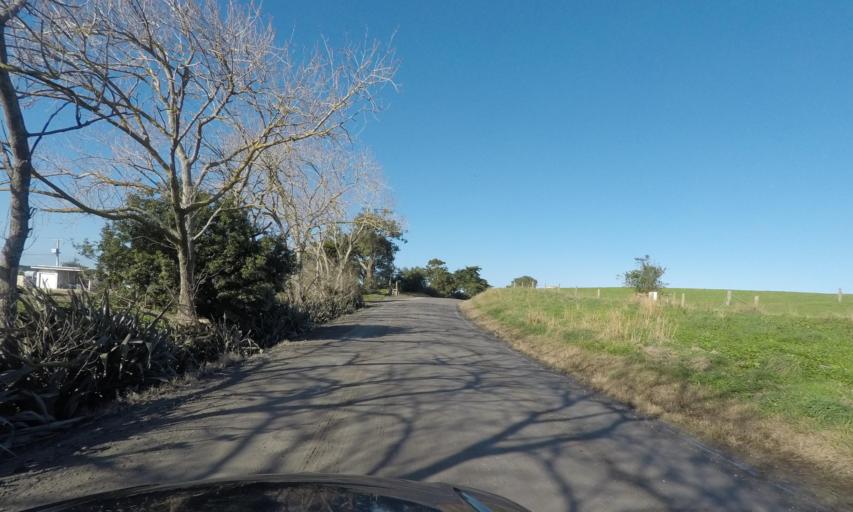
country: NZ
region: Auckland
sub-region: Auckland
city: Wellsford
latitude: -36.1556
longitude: 174.6020
